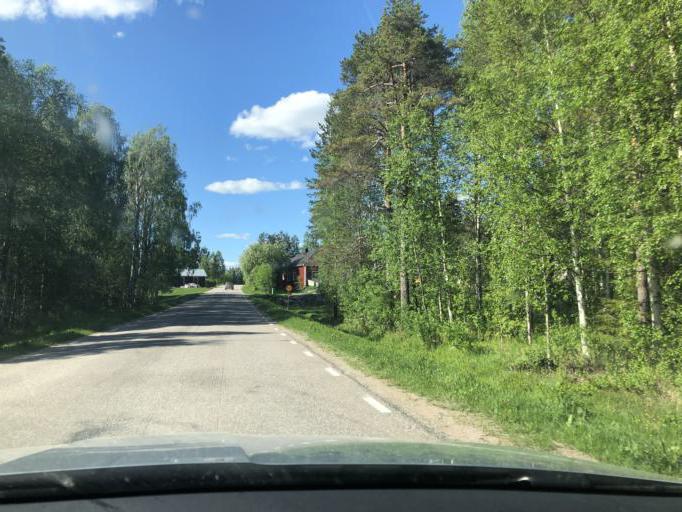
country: SE
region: Norrbotten
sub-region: Kalix Kommun
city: Kalix
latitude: 65.9236
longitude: 23.1669
